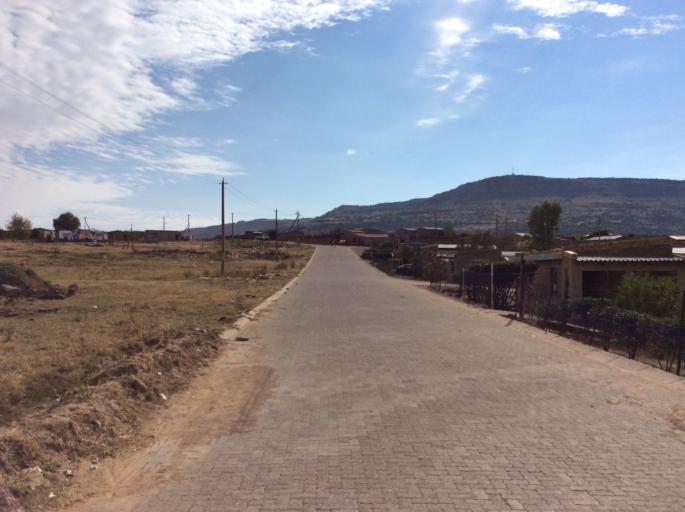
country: LS
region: Mafeteng
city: Mafeteng
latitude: -29.7208
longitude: 27.0167
